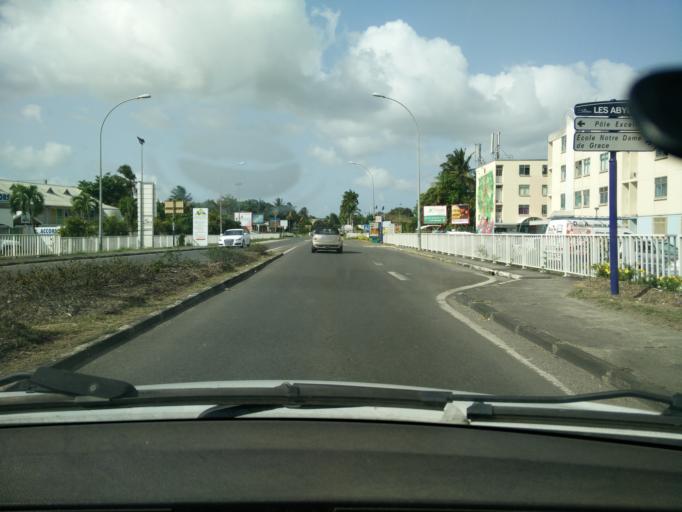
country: GP
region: Guadeloupe
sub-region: Guadeloupe
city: Les Abymes
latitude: 16.2569
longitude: -61.5204
